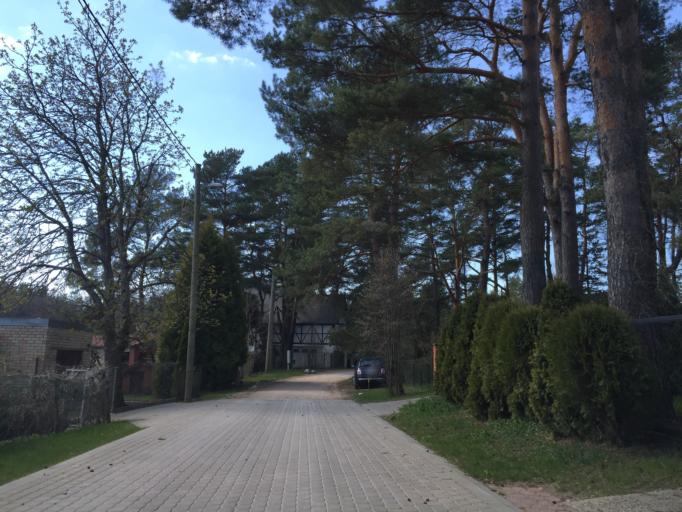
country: LV
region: Saulkrastu
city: Saulkrasti
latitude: 57.2305
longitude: 24.3910
